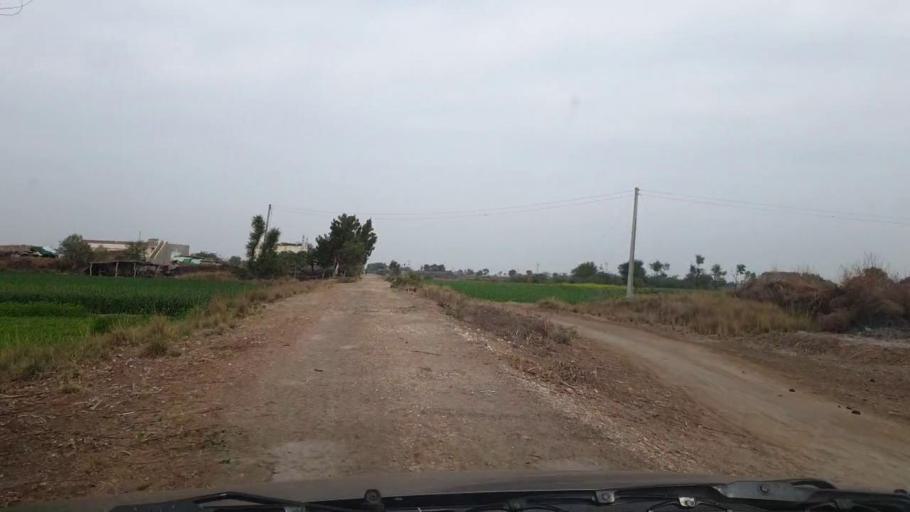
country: PK
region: Sindh
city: Sanghar
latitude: 26.1062
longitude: 68.8963
